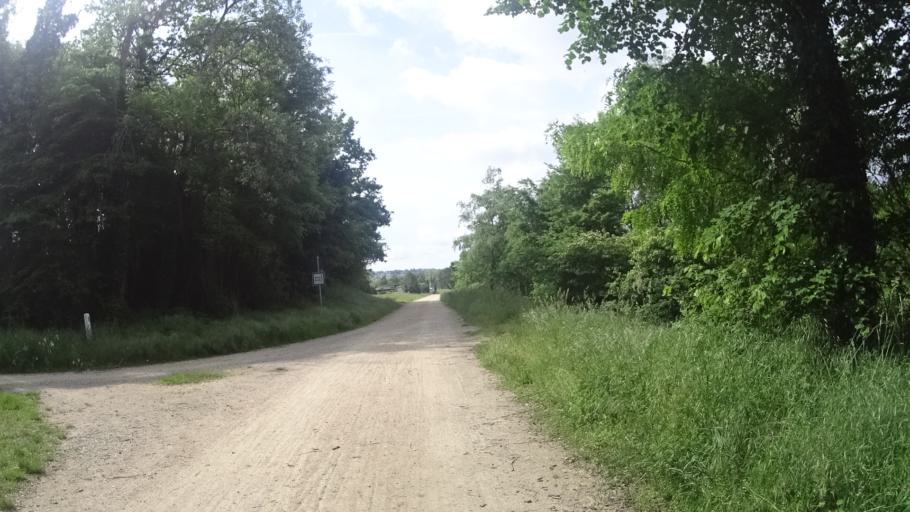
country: DE
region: Baden-Wuerttemberg
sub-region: Freiburg Region
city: Bad Bellingen
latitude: 47.7376
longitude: 7.5500
